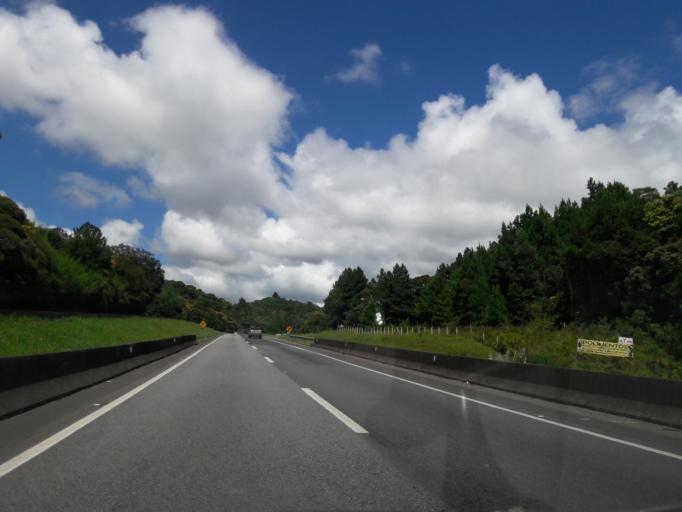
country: BR
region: Parana
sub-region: Campina Grande Do Sul
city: Campina Grande do Sul
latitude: -25.1706
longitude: -48.8674
